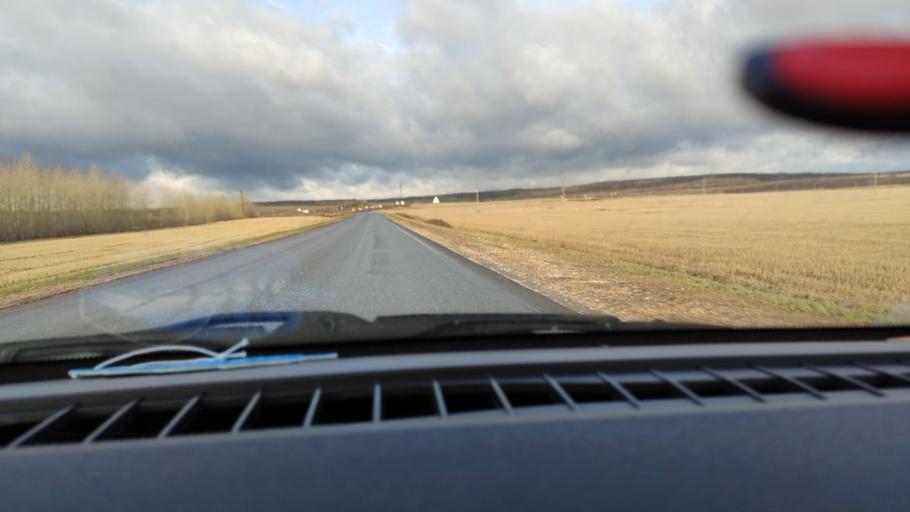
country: RU
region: Tatarstan
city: Russkiy Aktash
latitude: 55.0393
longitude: 52.0458
